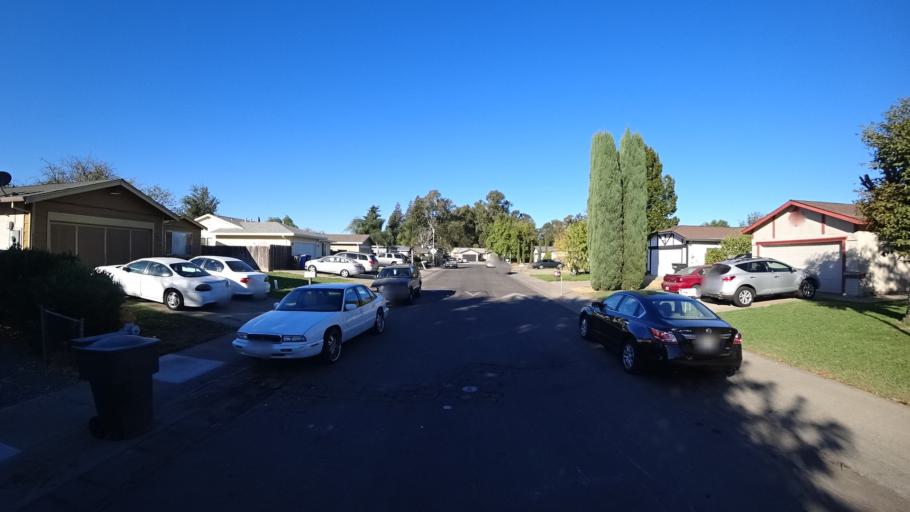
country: US
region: California
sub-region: Sacramento County
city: Parkway
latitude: 38.4853
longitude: -121.4621
